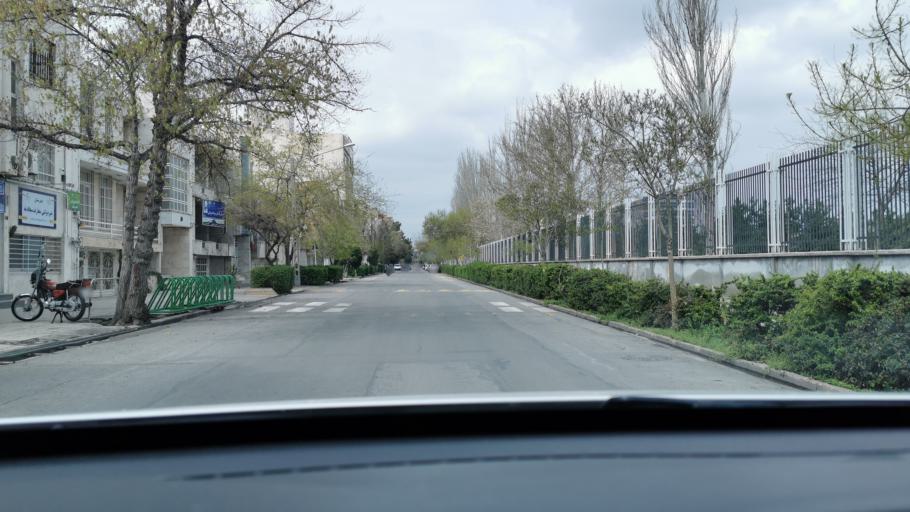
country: IR
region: Razavi Khorasan
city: Mashhad
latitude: 36.2859
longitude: 59.5790
